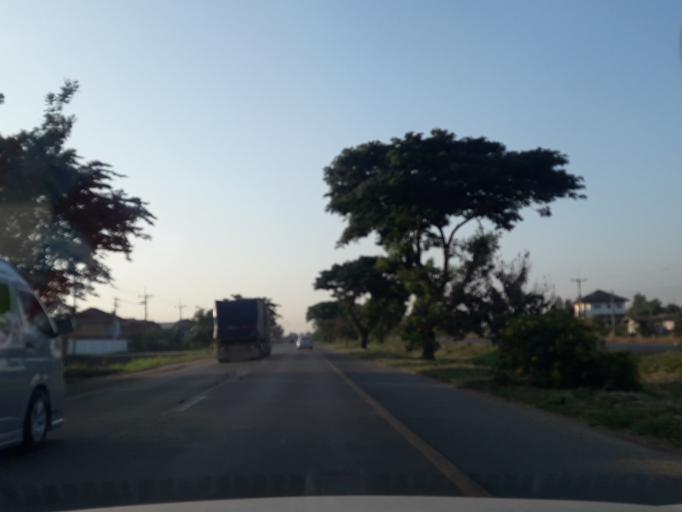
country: TH
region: Phra Nakhon Si Ayutthaya
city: Bang Pa-in
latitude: 14.2333
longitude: 100.5392
